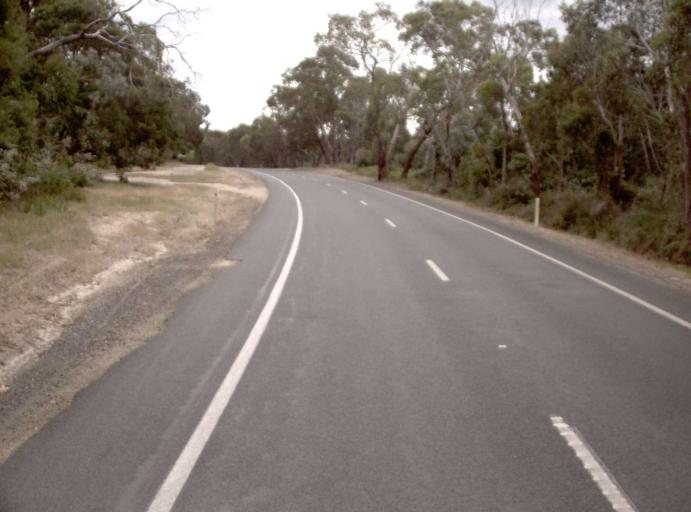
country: AU
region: Victoria
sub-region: Wellington
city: Sale
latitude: -38.2473
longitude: 147.0556
